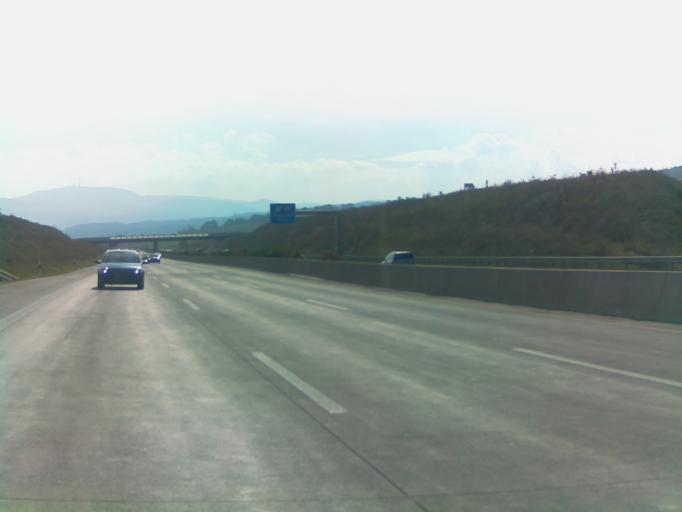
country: DE
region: Thuringia
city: Haina
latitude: 50.9620
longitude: 10.4882
